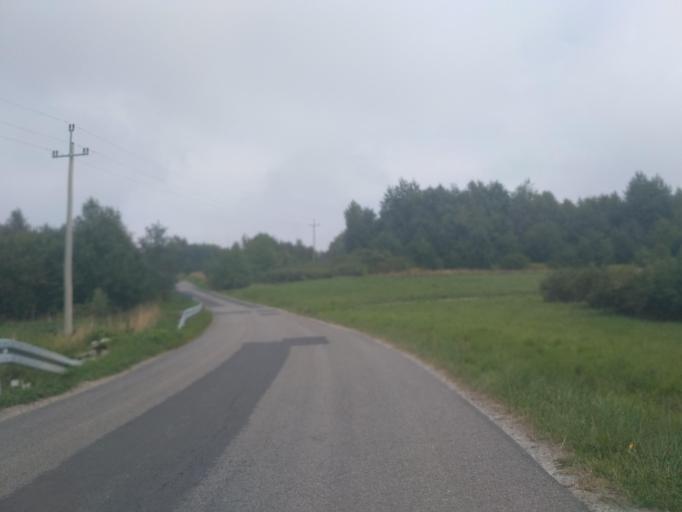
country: PL
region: Subcarpathian Voivodeship
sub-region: Powiat rzeszowski
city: Chmielnik
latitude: 50.0083
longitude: 22.1261
